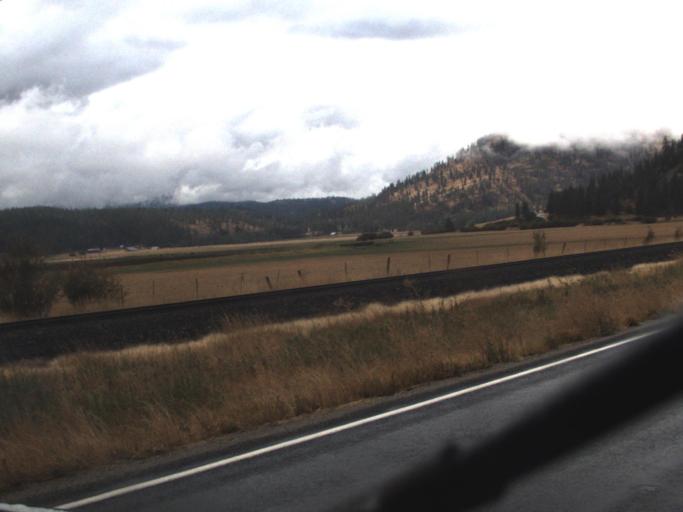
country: US
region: Washington
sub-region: Stevens County
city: Chewelah
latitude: 48.1868
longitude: -117.7321
